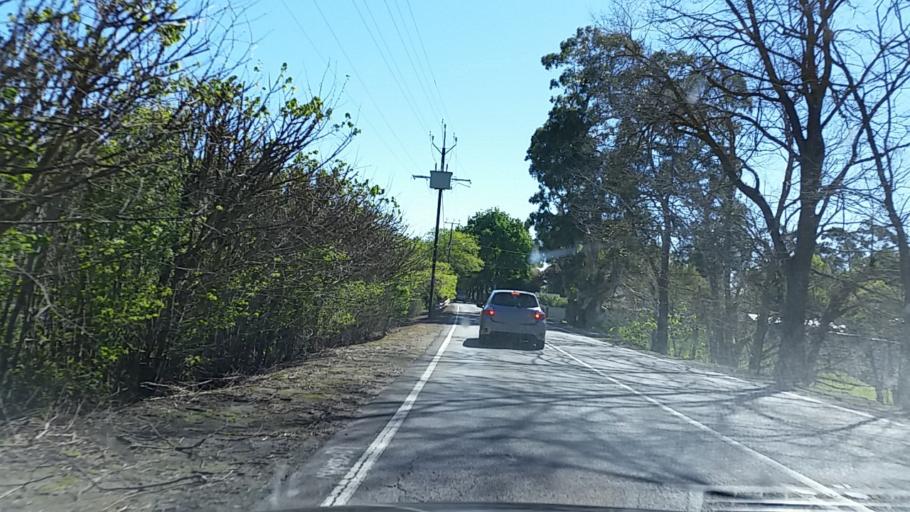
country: AU
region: South Australia
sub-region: Mount Barker
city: Meadows
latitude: -35.1805
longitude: 138.7657
